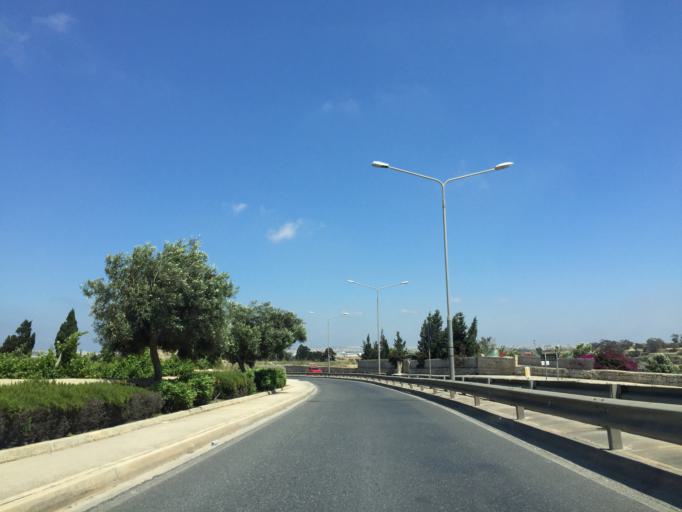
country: MT
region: L-Imdina
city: Imdina
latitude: 35.8907
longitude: 14.4060
